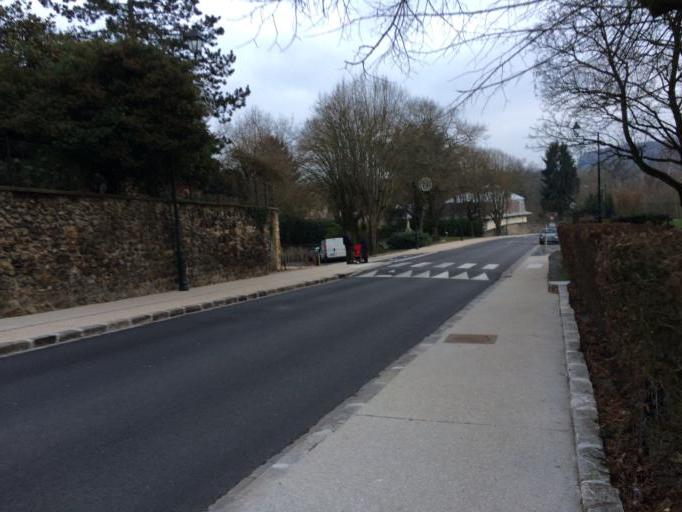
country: FR
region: Ile-de-France
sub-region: Departement de l'Essonne
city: Bievres
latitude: 48.7546
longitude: 2.2153
